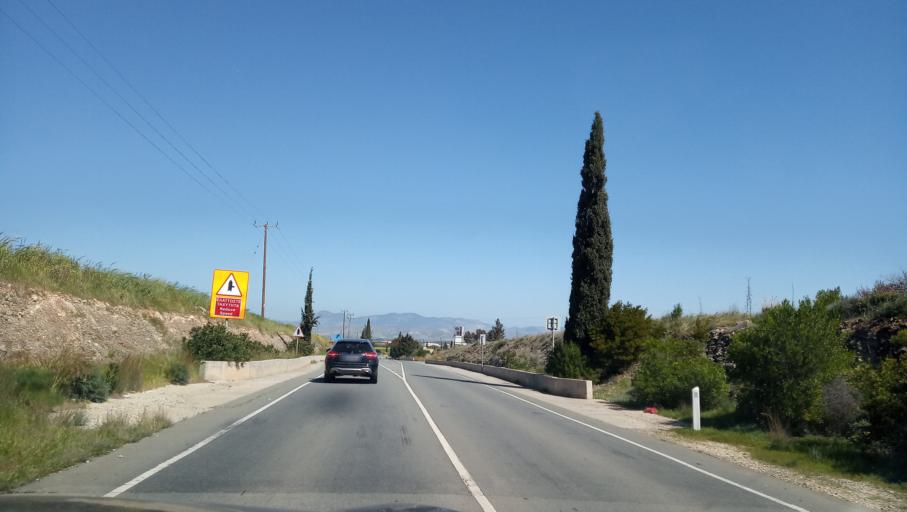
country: CY
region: Lefkosia
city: Astromeritis
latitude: 35.1262
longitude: 33.0120
